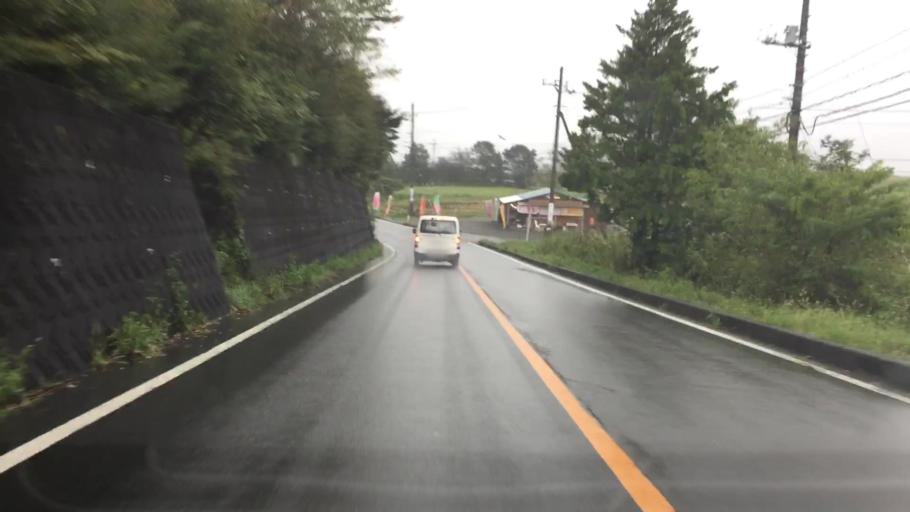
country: JP
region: Yamanashi
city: Fujikawaguchiko
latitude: 35.4207
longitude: 138.6244
